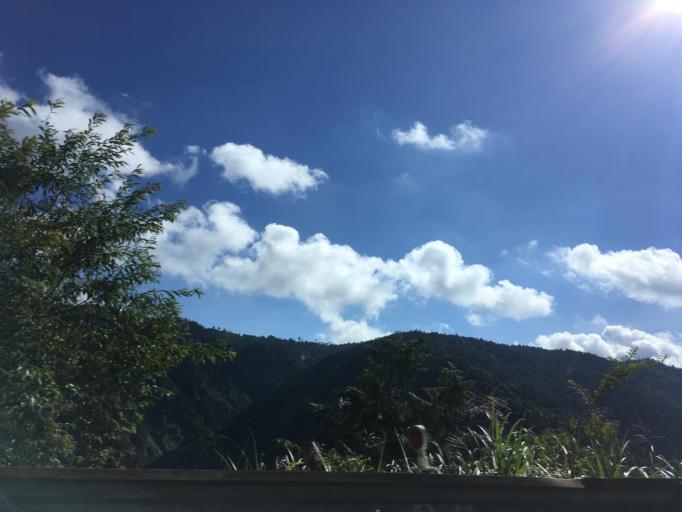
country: TW
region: Taiwan
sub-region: Yilan
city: Yilan
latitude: 24.5099
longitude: 121.5696
